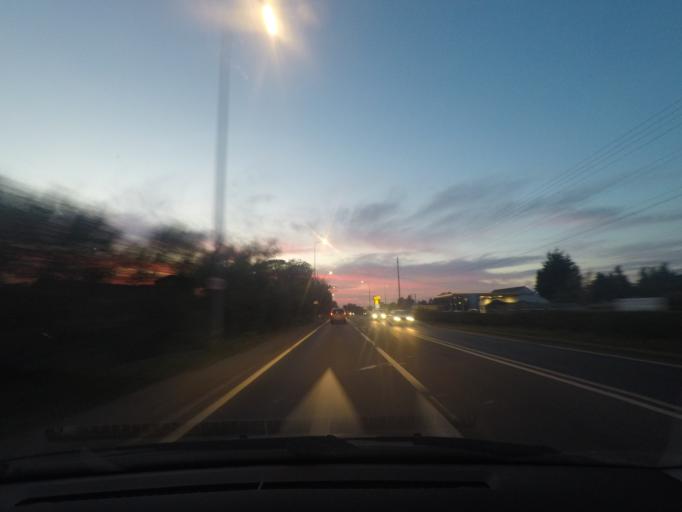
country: GB
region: England
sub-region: East Riding of Yorkshire
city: Thornton
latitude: 53.9327
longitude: -0.8361
